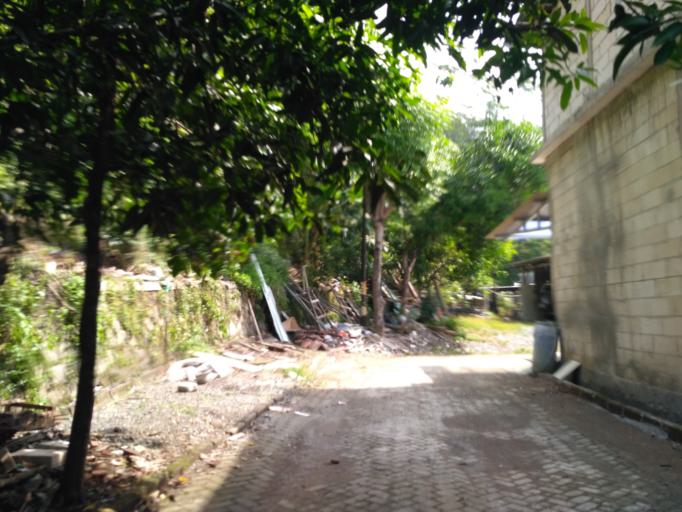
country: ID
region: Central Java
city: Semarang
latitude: -7.0461
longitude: 110.4448
